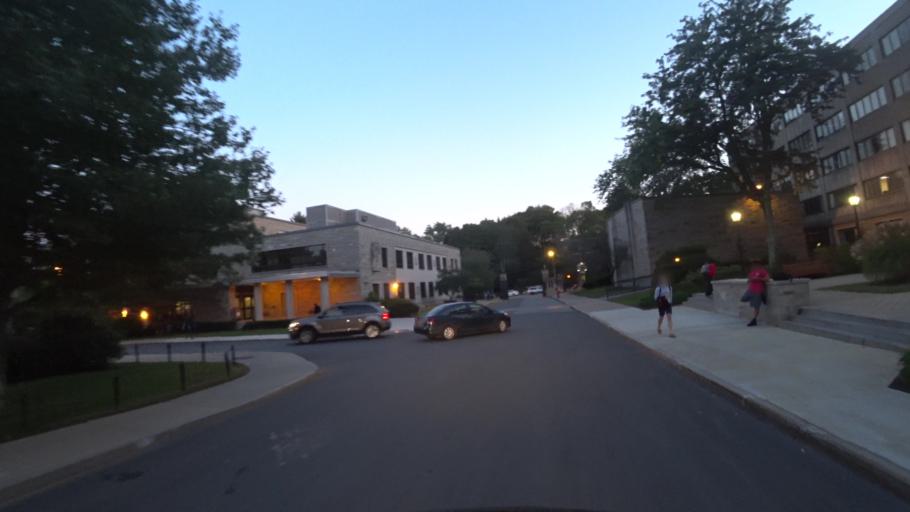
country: US
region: Massachusetts
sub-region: Middlesex County
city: Watertown
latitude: 42.3341
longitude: -71.1693
